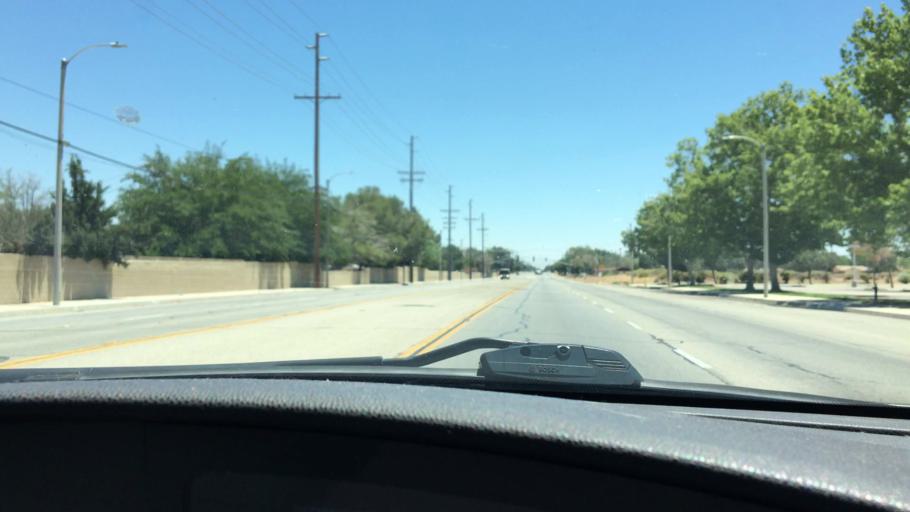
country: US
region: California
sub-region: Los Angeles County
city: Quartz Hill
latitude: 34.6602
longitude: -118.1959
